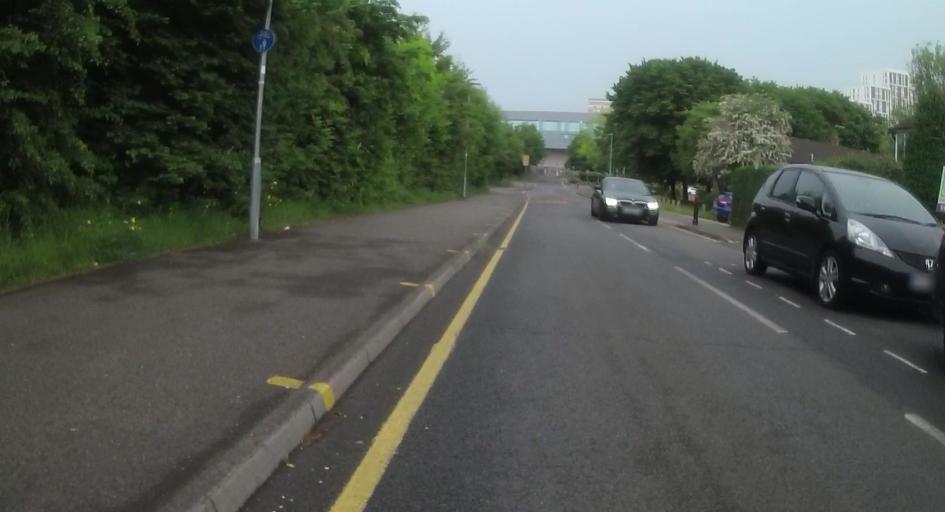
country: GB
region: England
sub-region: Bracknell Forest
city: Bracknell
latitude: 51.4204
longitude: -0.7510
